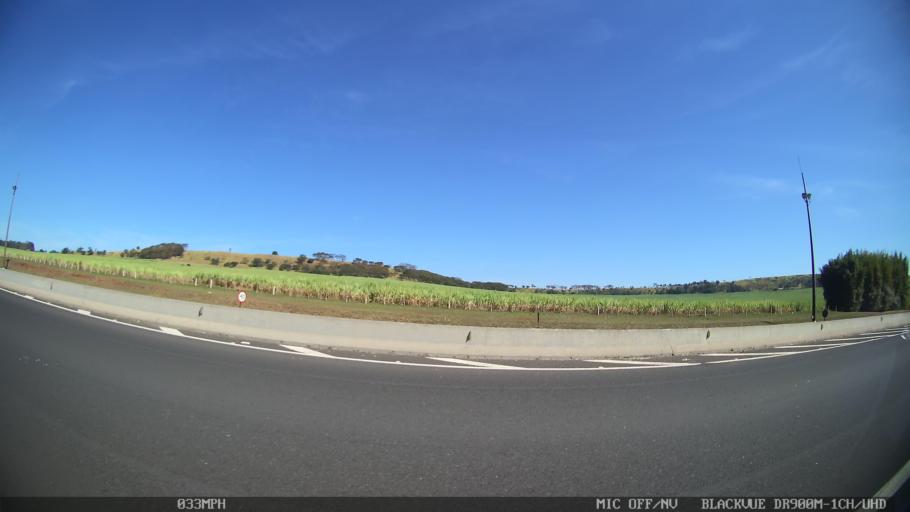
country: BR
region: Sao Paulo
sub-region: Cravinhos
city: Cravinhos
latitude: -21.4126
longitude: -47.6657
